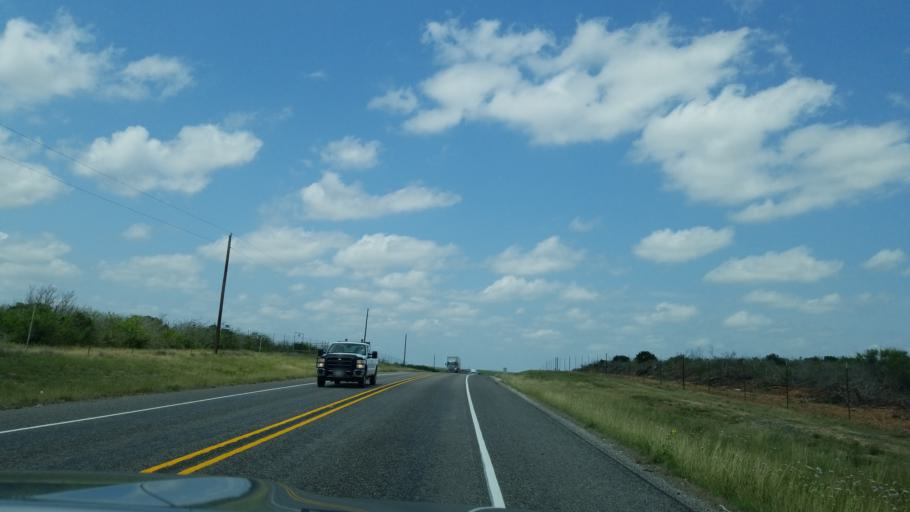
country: US
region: Texas
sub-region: Frio County
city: Pearsall
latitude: 28.9445
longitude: -99.3016
